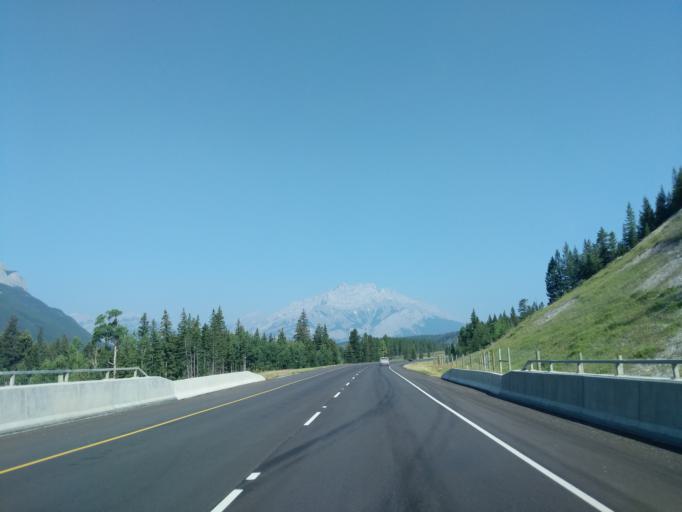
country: CA
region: Alberta
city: Canmore
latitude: 51.1501
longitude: -115.4285
